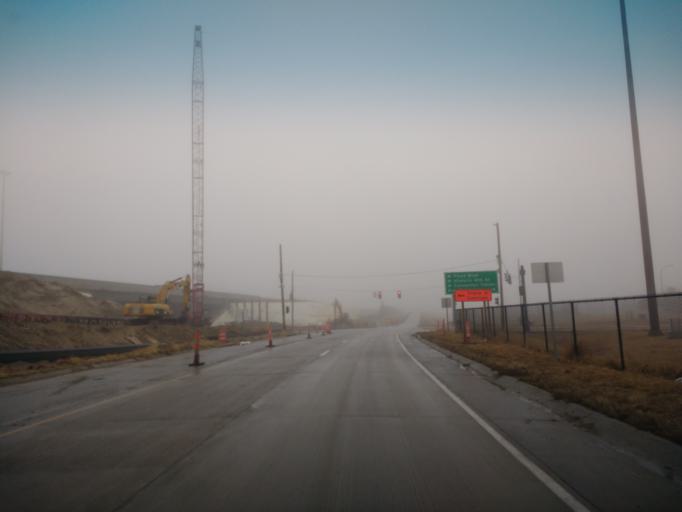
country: US
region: Iowa
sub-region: Woodbury County
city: Sioux City
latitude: 42.4871
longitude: -96.3965
